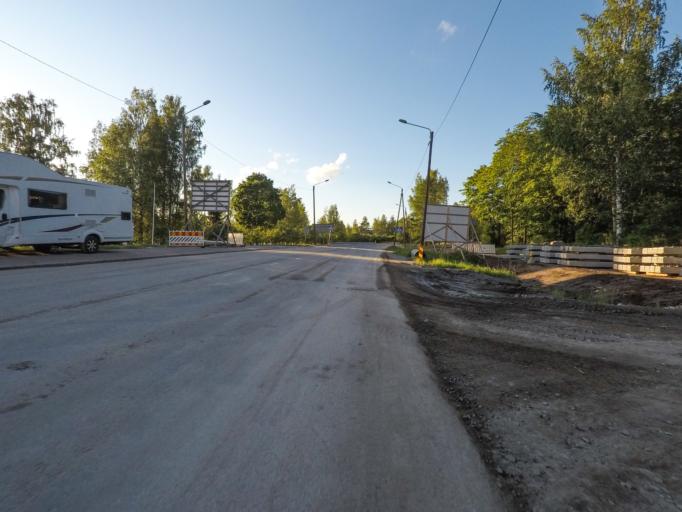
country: FI
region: South Karelia
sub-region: Imatra
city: Imatra
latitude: 61.1983
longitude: 28.7836
